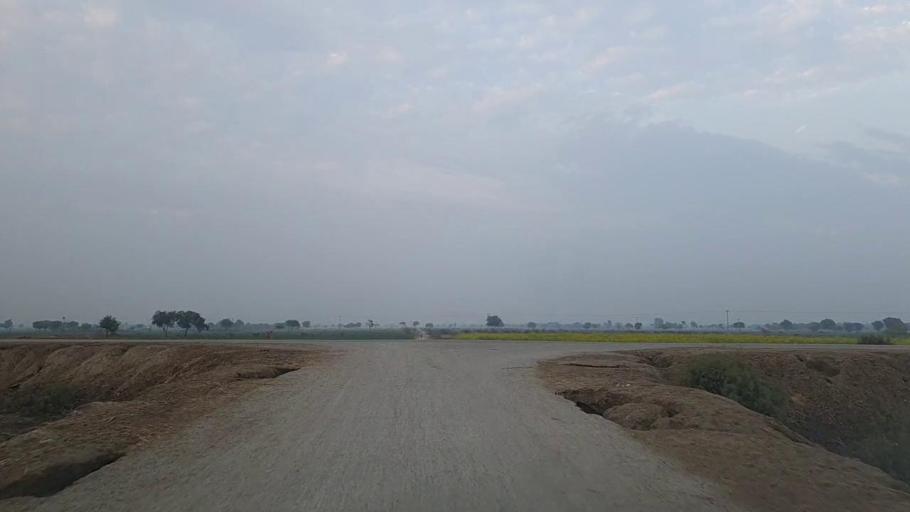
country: PK
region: Sindh
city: Jam Sahib
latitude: 26.3085
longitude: 68.5937
